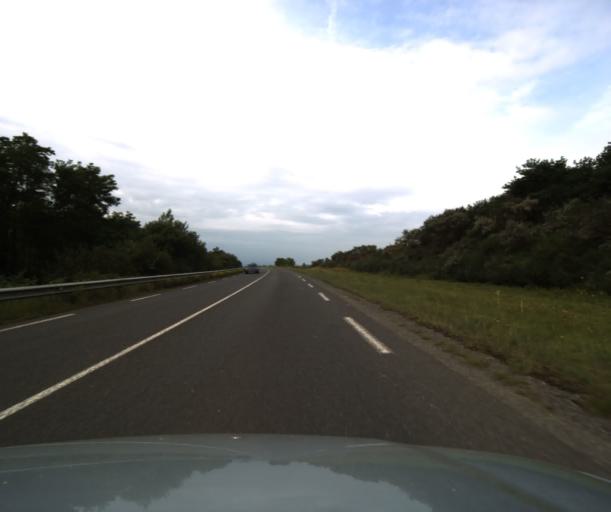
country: FR
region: Midi-Pyrenees
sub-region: Departement des Hautes-Pyrenees
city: Juillan
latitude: 43.2207
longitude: 0.0193
